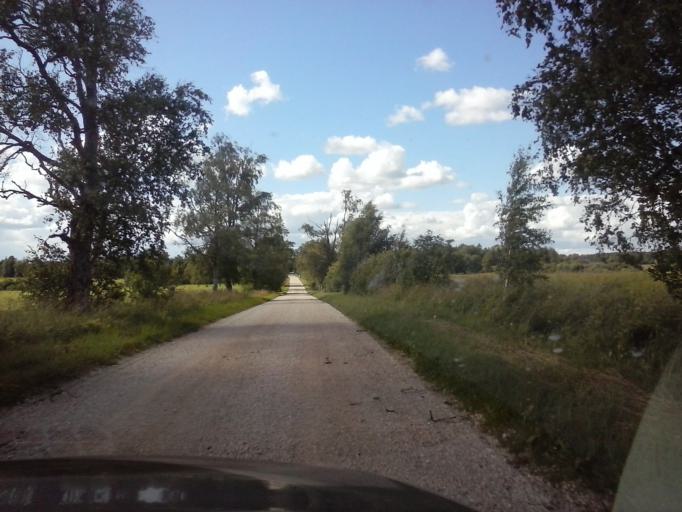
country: EE
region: Laeaene-Virumaa
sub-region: Vaeike-Maarja vald
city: Vaike-Maarja
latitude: 59.0827
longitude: 26.1899
